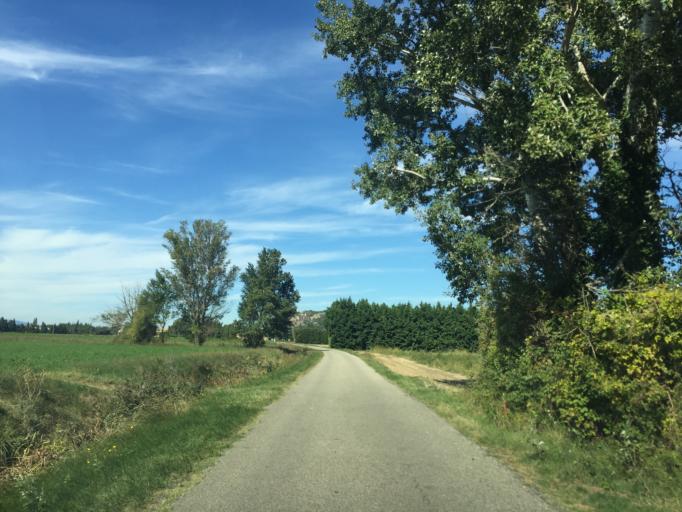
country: FR
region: Provence-Alpes-Cote d'Azur
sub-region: Departement du Vaucluse
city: Mornas
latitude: 44.1851
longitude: 4.7339
